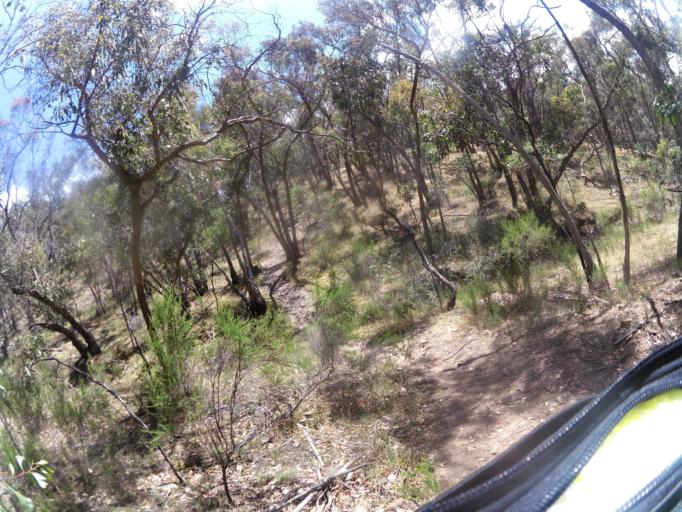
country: AU
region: Victoria
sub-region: Mount Alexander
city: Castlemaine
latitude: -37.0625
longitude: 144.2672
